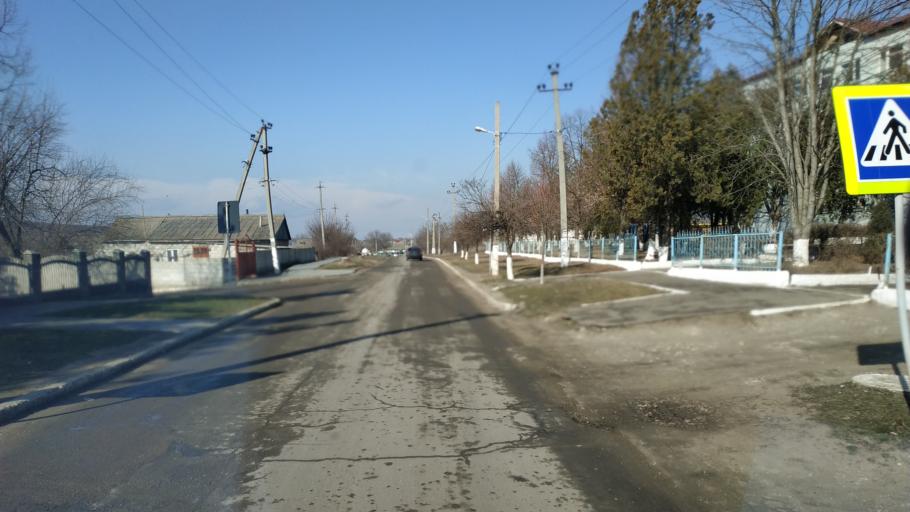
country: MD
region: Chisinau
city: Singera
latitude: 46.6852
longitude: 29.0545
